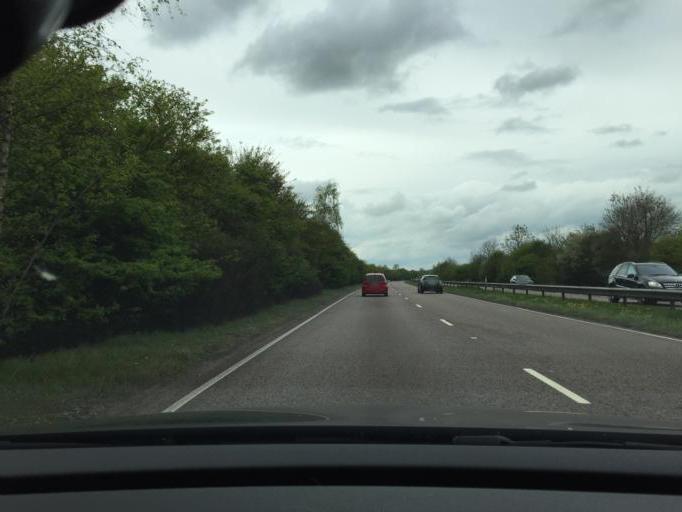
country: GB
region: England
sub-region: West Berkshire
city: Newbury
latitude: 51.4280
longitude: -1.3243
